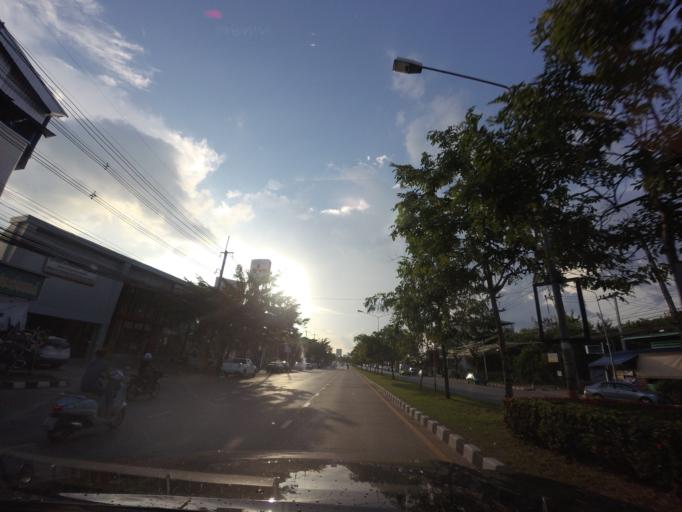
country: TH
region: Khon Kaen
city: Khon Kaen
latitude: 16.4284
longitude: 102.8563
